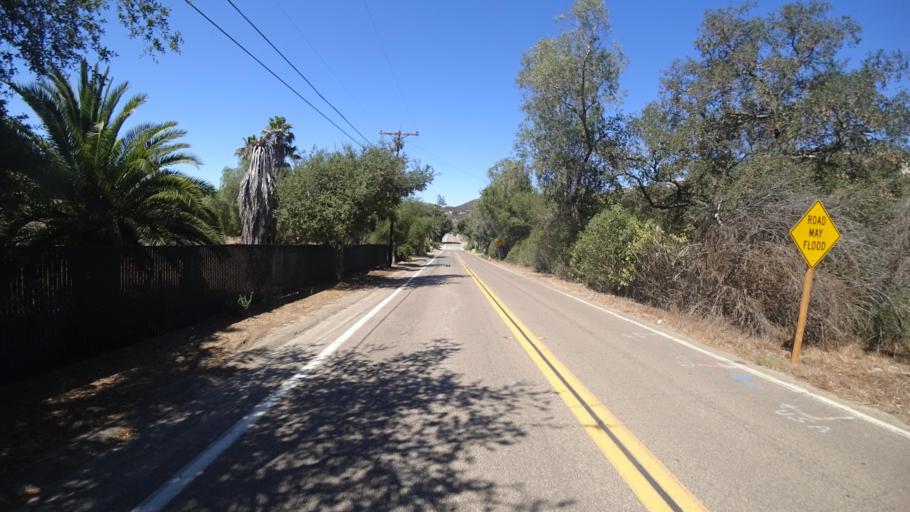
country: US
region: California
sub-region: San Diego County
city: Rainbow
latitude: 33.4139
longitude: -117.1549
